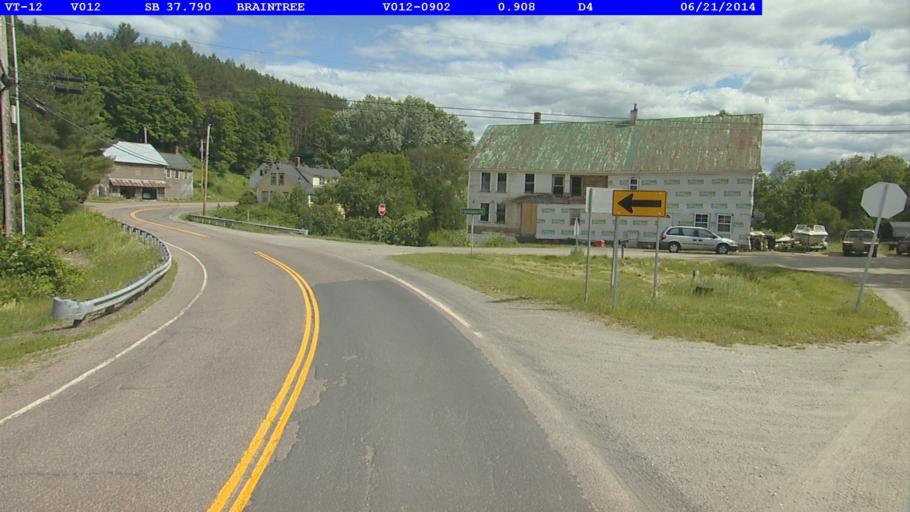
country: US
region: Vermont
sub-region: Orange County
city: Randolph
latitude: 43.9963
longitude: -72.6521
